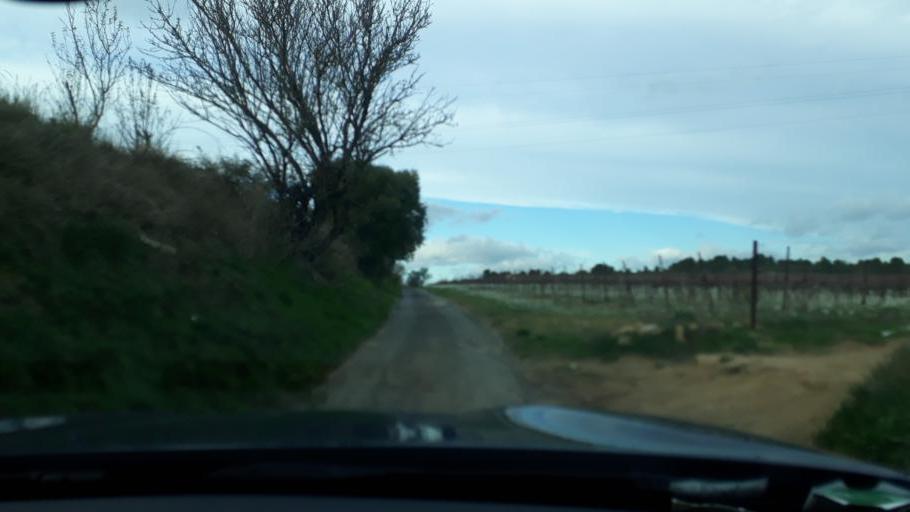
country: FR
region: Languedoc-Roussillon
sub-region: Departement de l'Herault
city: Florensac
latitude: 43.4118
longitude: 3.4588
